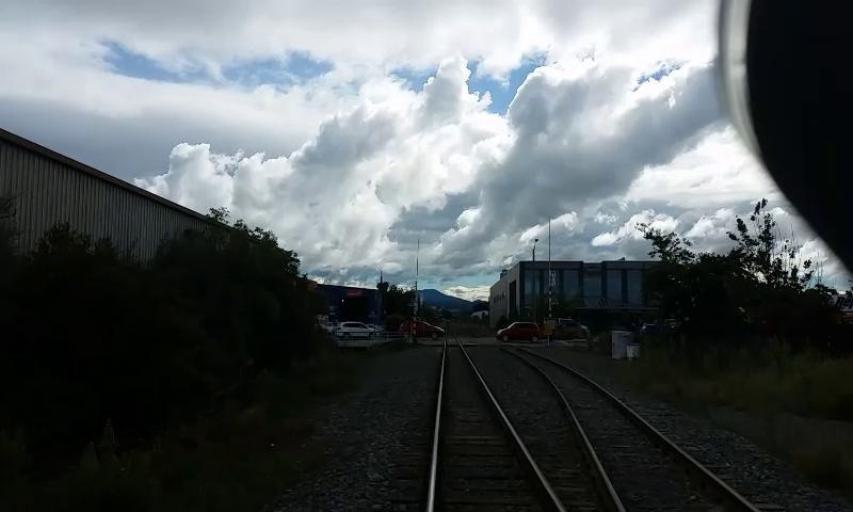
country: NZ
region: Canterbury
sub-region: Waimakariri District
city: Woodend
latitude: -43.3036
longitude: 172.5984
